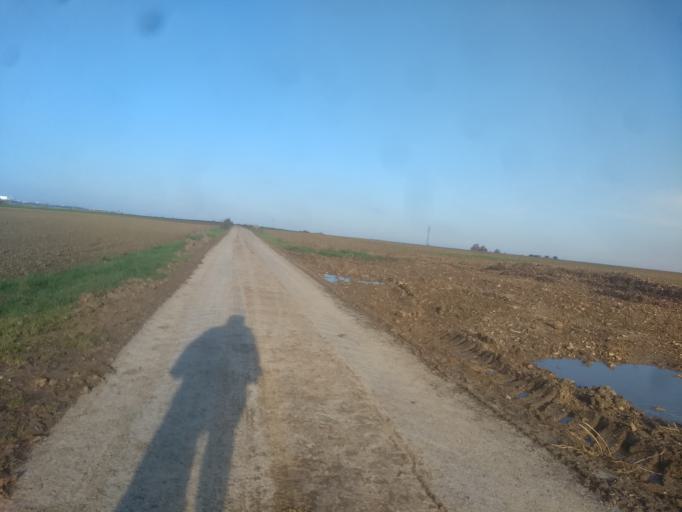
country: FR
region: Nord-Pas-de-Calais
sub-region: Departement du Pas-de-Calais
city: Tilloy-les-Mofflaines
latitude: 50.2808
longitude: 2.8214
